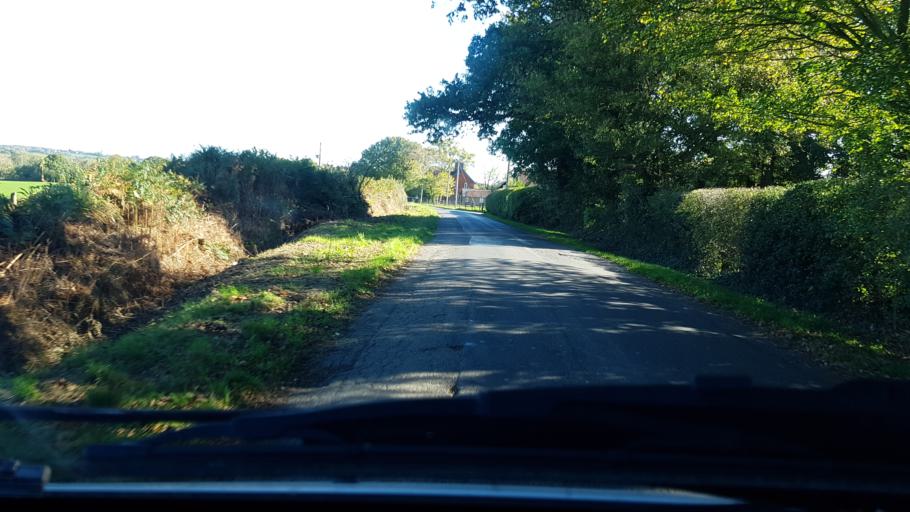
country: GB
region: England
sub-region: Surrey
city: Ockley
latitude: 51.1235
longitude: -0.3747
